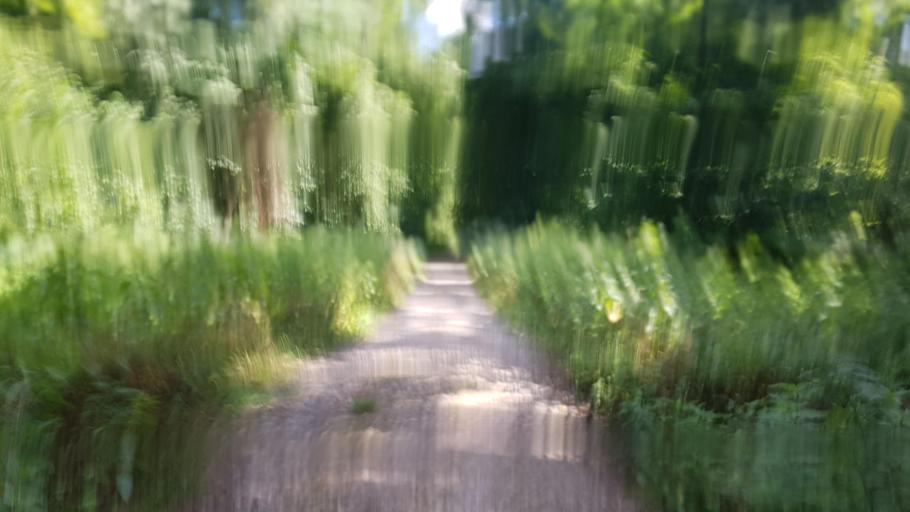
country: DE
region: Baden-Wuerttemberg
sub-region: Karlsruhe Region
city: Karlsdorf-Neuthard
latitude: 49.1000
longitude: 8.5540
